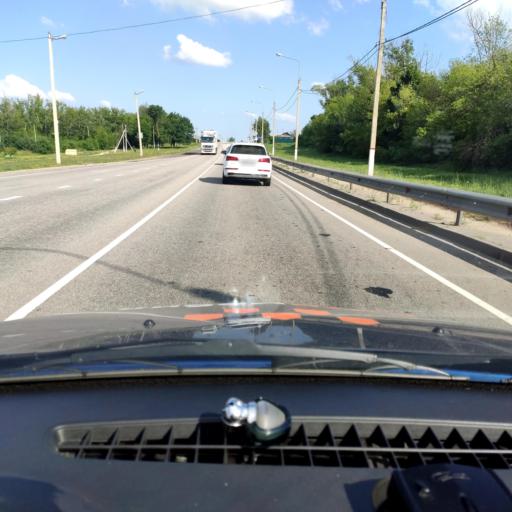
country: RU
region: Lipetsk
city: Yelets
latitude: 52.5568
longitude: 38.6969
